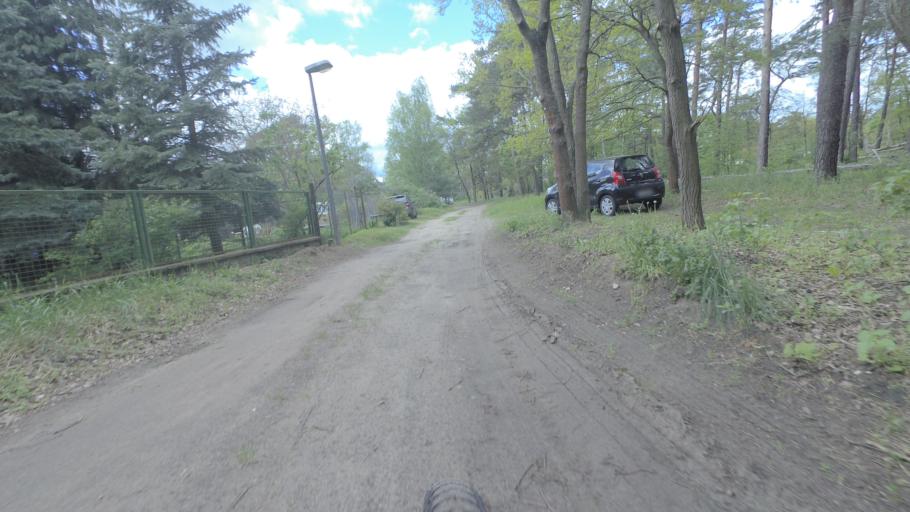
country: DE
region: Brandenburg
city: Ludwigsfelde
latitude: 52.3181
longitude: 13.2383
